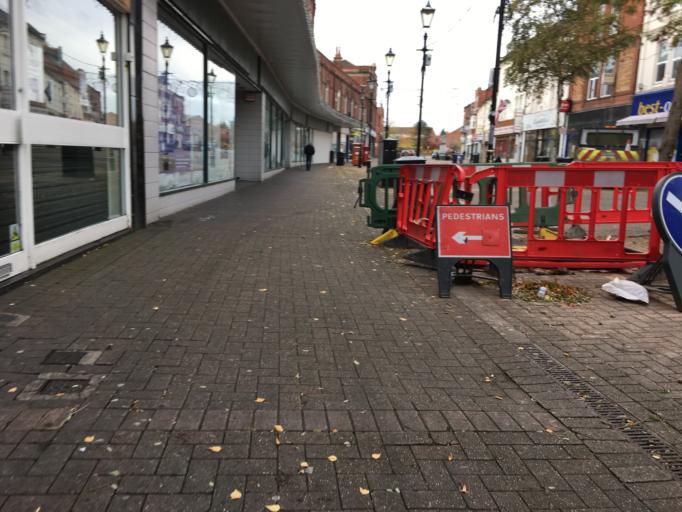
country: GB
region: England
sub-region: Warwickshire
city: Nuneaton
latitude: 52.5235
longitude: -1.4696
